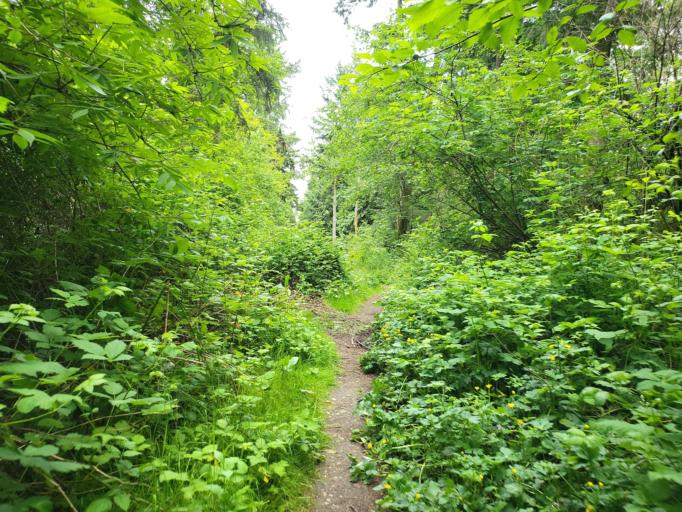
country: US
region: Washington
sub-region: Pierce County
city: Fife Heights
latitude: 47.3152
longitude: -122.3983
